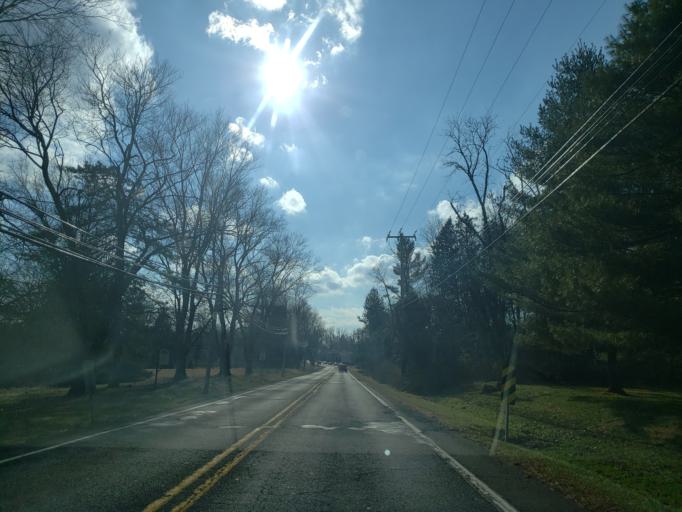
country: US
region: Pennsylvania
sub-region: Bucks County
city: Doylestown
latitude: 40.3392
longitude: -75.0456
